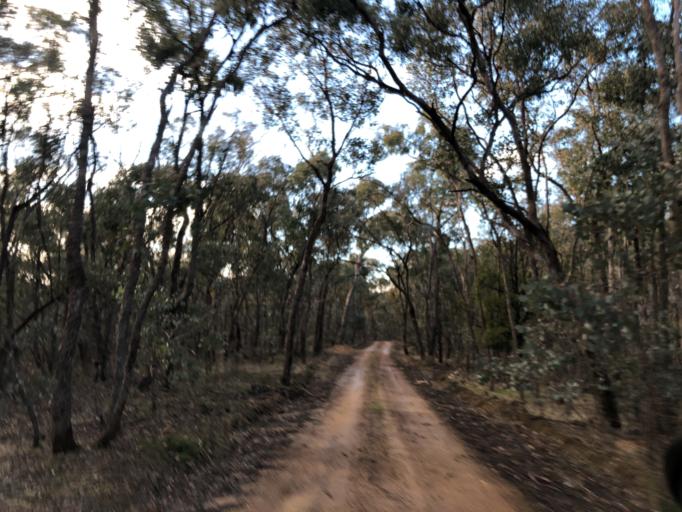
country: AU
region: Victoria
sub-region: Mount Alexander
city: Castlemaine
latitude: -37.2225
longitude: 144.2642
